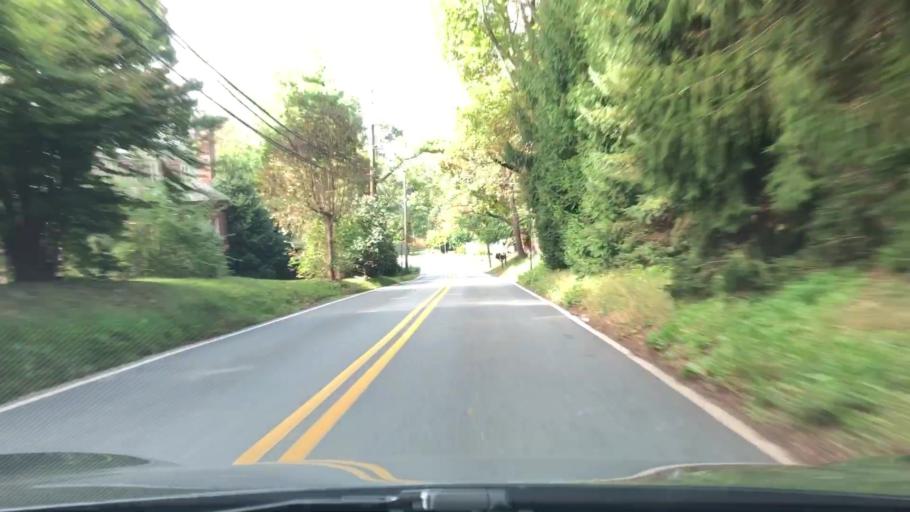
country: US
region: Pennsylvania
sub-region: Delaware County
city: Wayne
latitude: 40.0146
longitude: -75.3726
